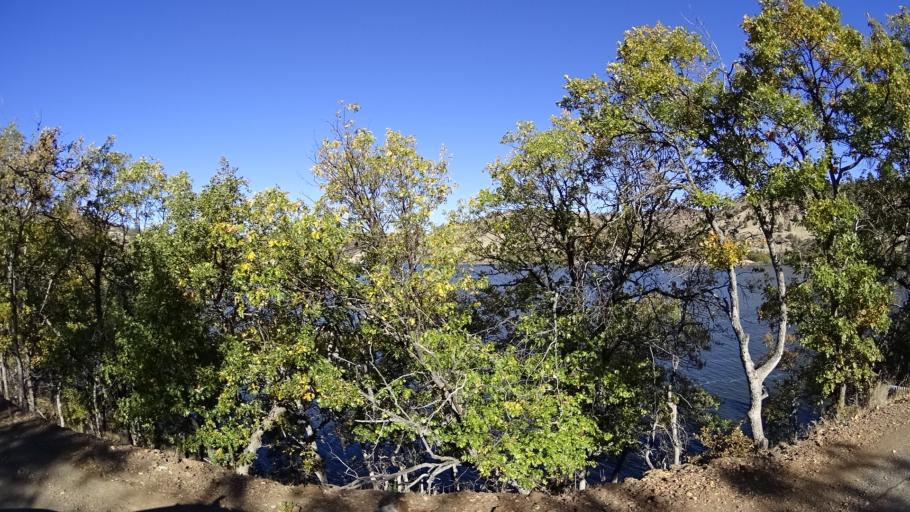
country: US
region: California
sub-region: Siskiyou County
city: Montague
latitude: 41.9744
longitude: -122.2952
